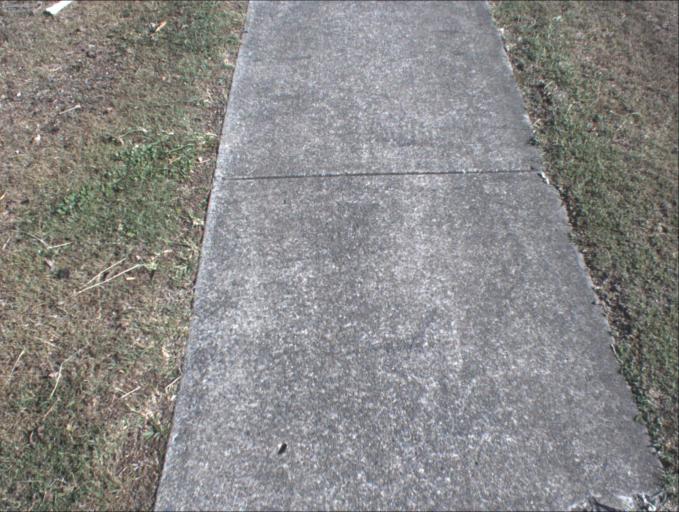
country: AU
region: Queensland
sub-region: Logan
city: Beenleigh
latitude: -27.7146
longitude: 153.1820
